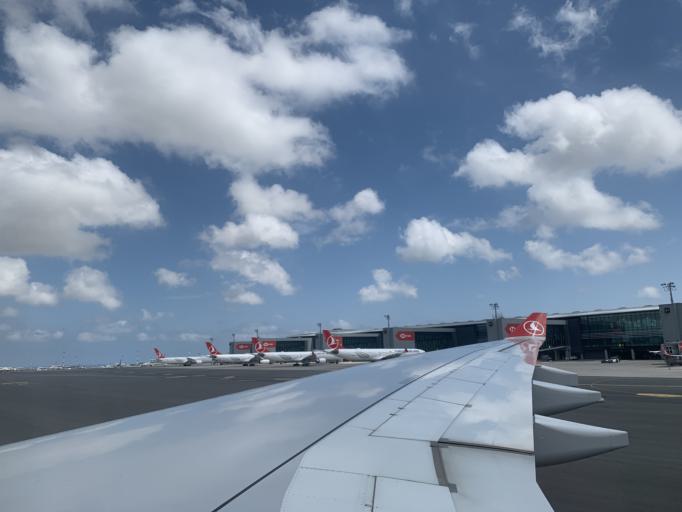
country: TR
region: Istanbul
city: Durusu
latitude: 41.2643
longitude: 28.7393
